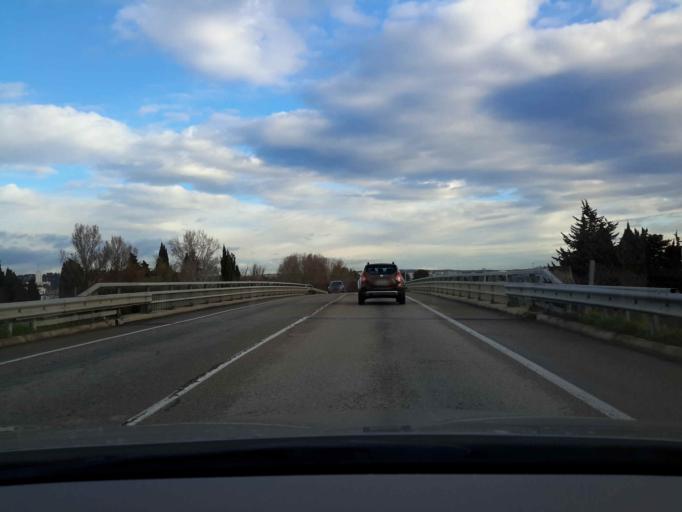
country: FR
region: Languedoc-Roussillon
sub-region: Departement du Gard
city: Nimes
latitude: 43.8073
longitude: 4.3543
